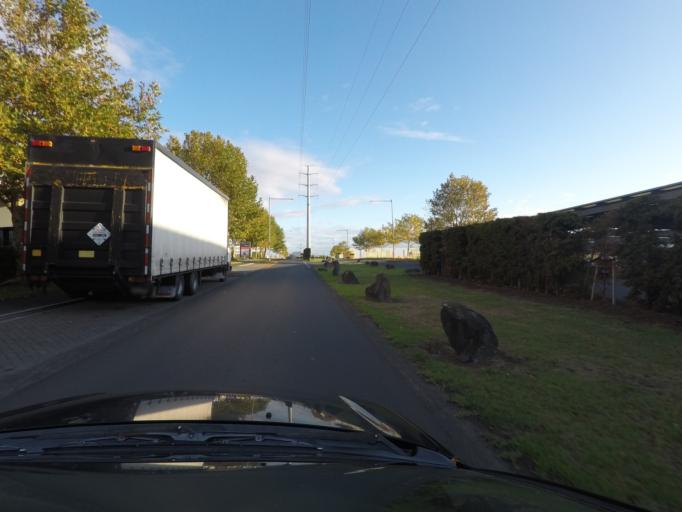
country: NZ
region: Auckland
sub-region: Auckland
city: Manukau City
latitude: -36.9420
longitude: 174.8728
